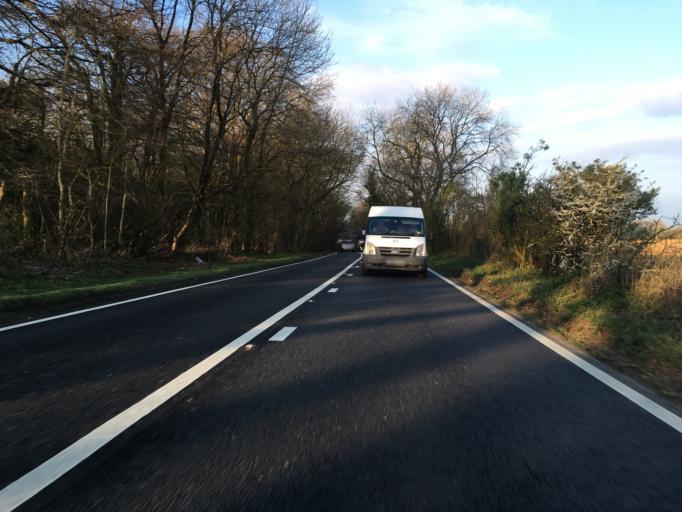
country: GB
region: England
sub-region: Gloucestershire
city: Charlton Kings
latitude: 51.8612
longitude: -2.0312
